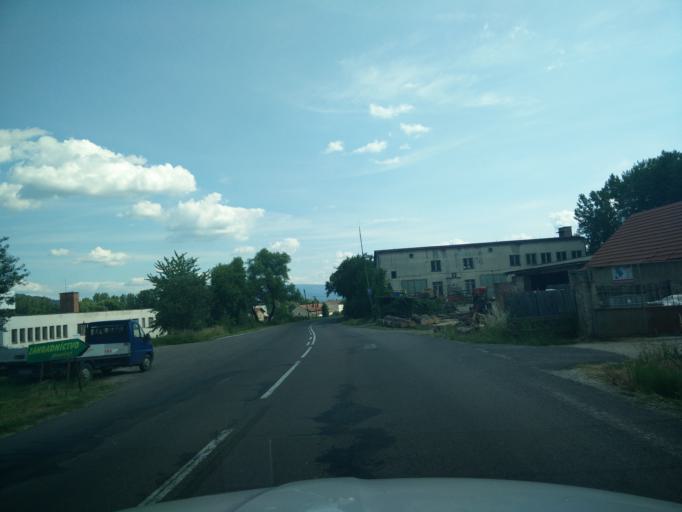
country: SK
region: Nitriansky
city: Prievidza
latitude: 48.8827
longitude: 18.6380
